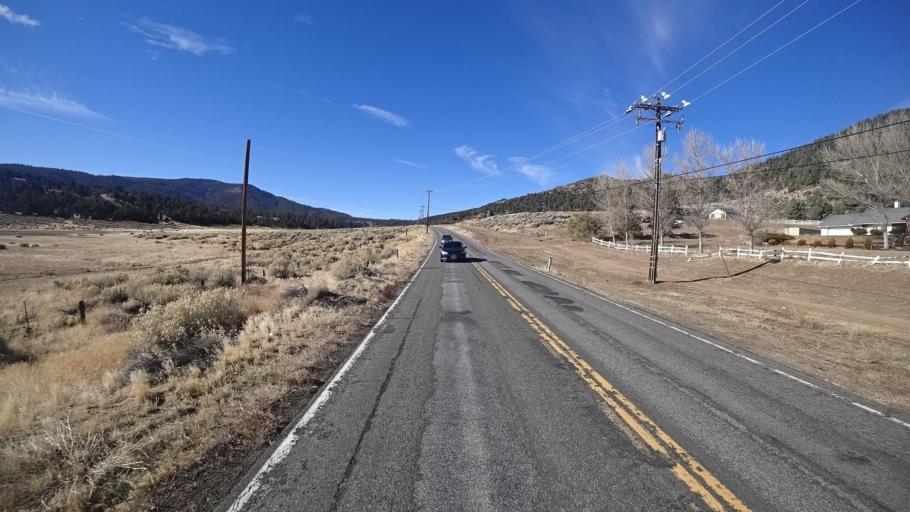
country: US
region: California
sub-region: Kern County
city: Frazier Park
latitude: 34.8370
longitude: -119.0440
